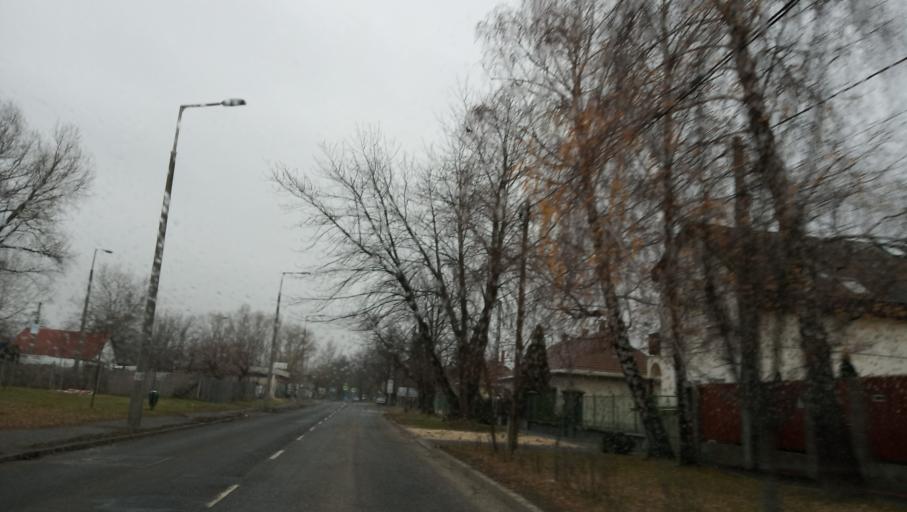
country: HU
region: Budapest
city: Budapest XV. keruelet
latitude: 47.5813
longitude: 19.1283
